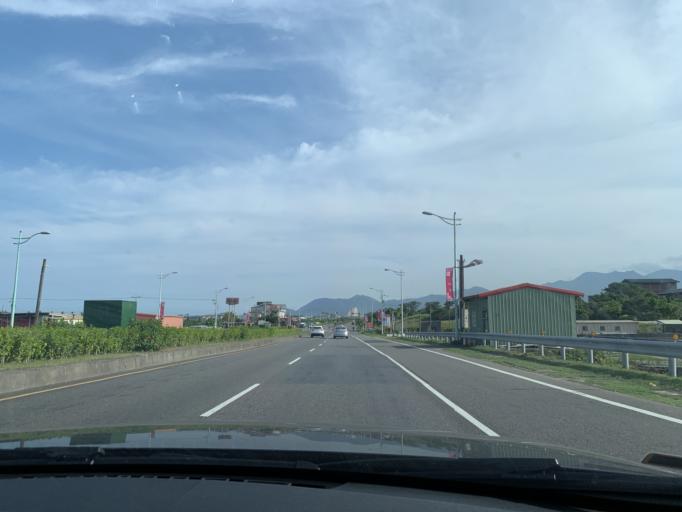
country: TW
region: Taiwan
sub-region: Yilan
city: Yilan
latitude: 24.6899
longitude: 121.8251
